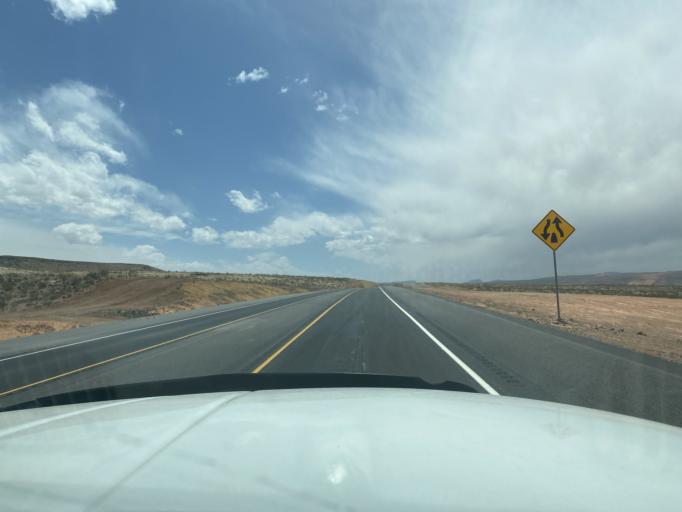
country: US
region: Utah
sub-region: Washington County
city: Hurricane
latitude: 37.1645
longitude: -113.3460
